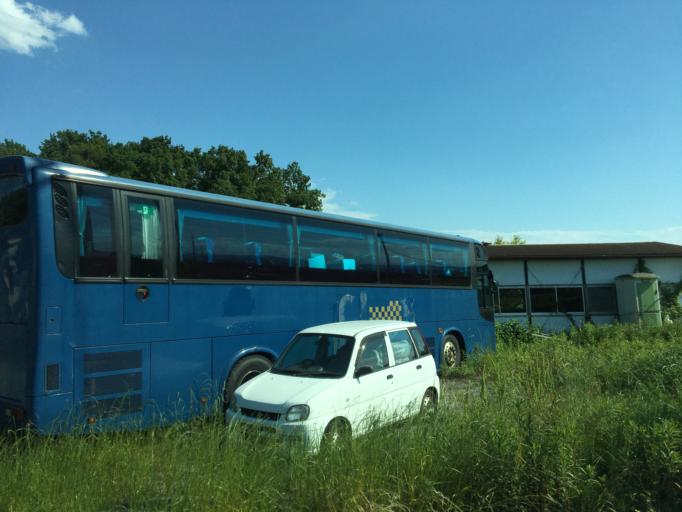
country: JP
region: Saitama
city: Sakado
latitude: 35.9655
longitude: 139.3494
